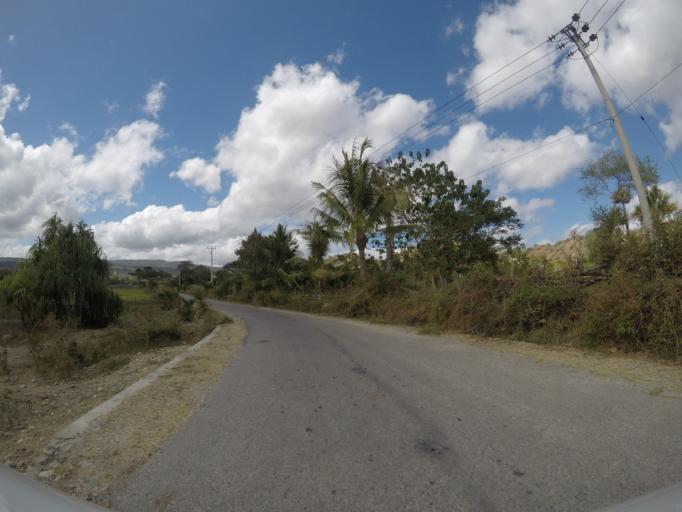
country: TL
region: Lautem
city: Lospalos
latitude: -8.4165
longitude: 126.8265
